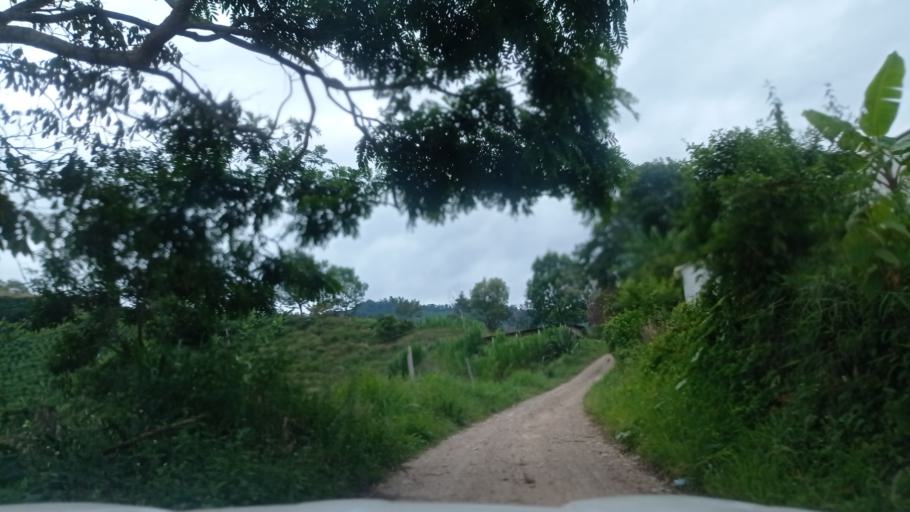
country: CO
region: Huila
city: Garzon
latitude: 2.0945
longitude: -75.6249
